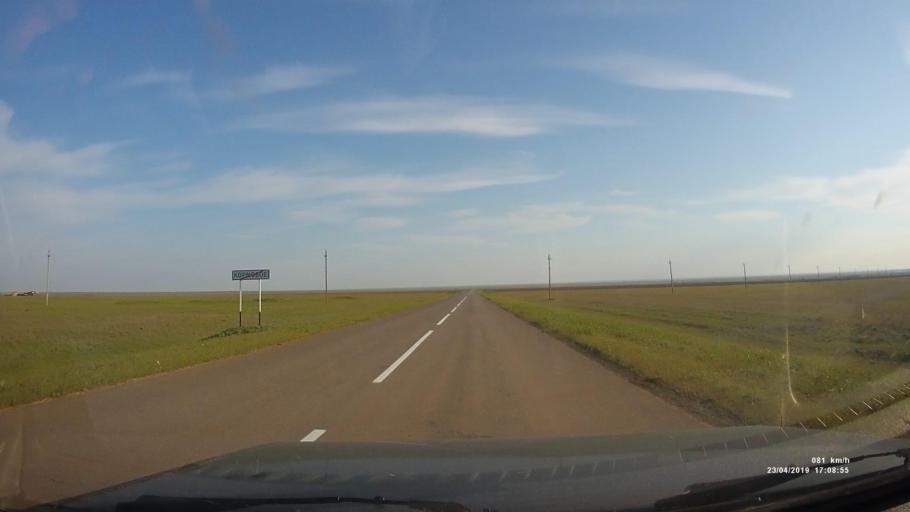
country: RU
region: Kalmykiya
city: Priyutnoye
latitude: 46.2655
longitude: 43.4844
